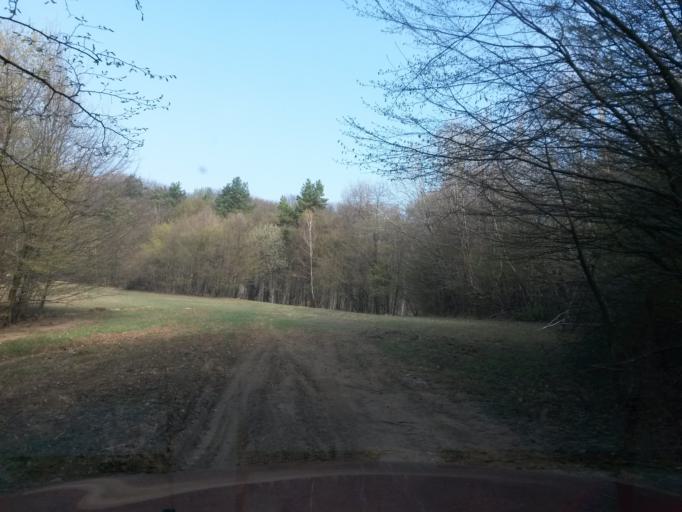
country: SK
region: Presovsky
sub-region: Okres Presov
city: Presov
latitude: 48.9244
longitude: 21.1643
